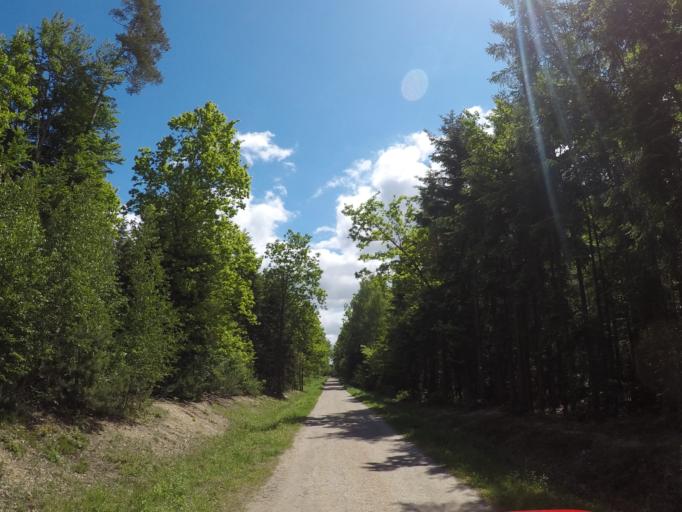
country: PL
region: Swietokrzyskie
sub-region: Powiat kielecki
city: Domaszowice
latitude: 50.9114
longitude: 20.6578
